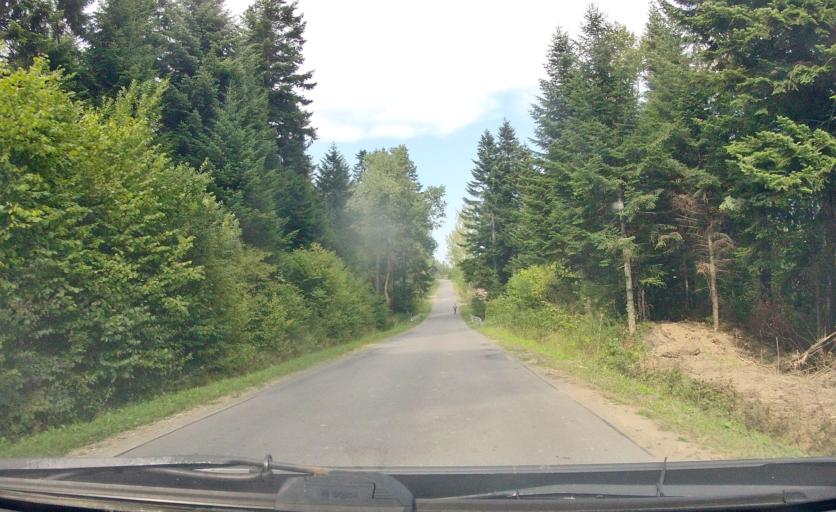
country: PL
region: Subcarpathian Voivodeship
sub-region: Powiat krosnienski
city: Dukla
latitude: 49.5024
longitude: 21.6220
